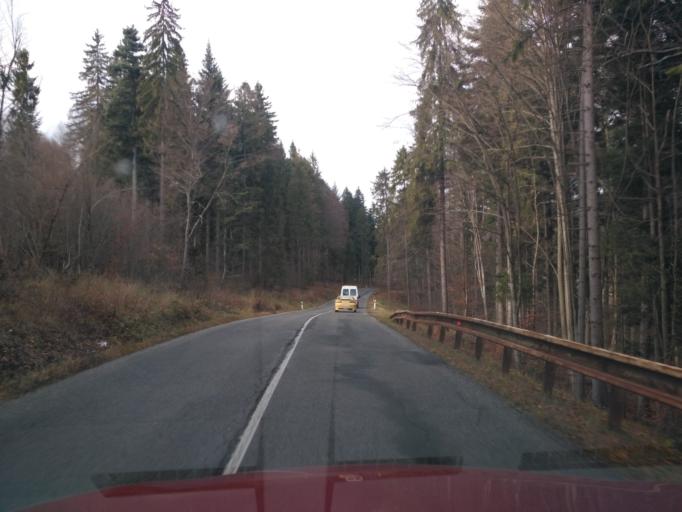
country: SK
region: Kosicky
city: Medzev
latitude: 48.7931
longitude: 20.7505
